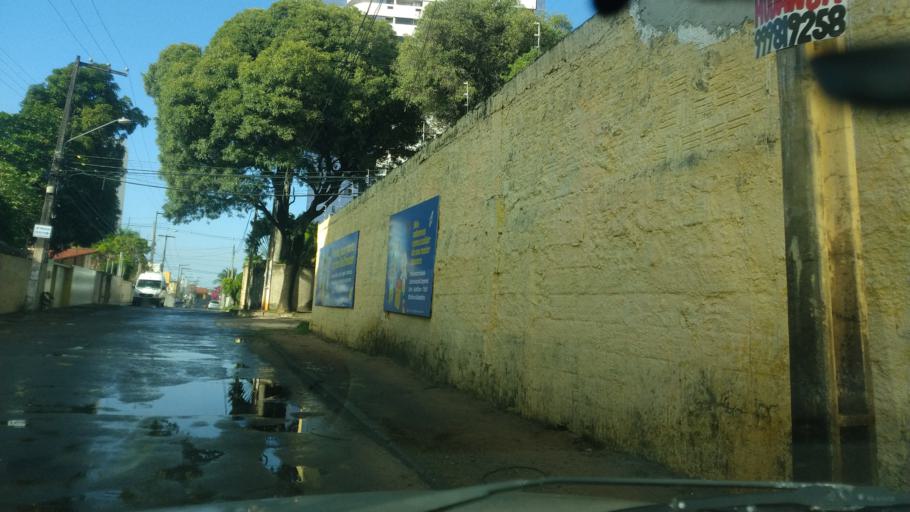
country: BR
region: Rio Grande do Norte
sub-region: Natal
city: Natal
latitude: -5.8526
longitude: -35.2048
